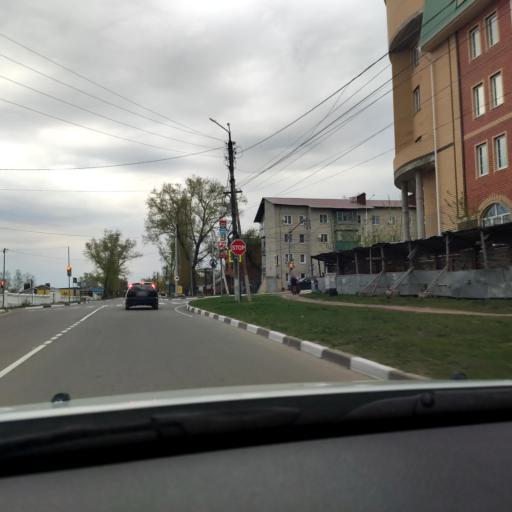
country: RU
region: Lipetsk
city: Zadonsk
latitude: 52.3929
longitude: 38.9162
